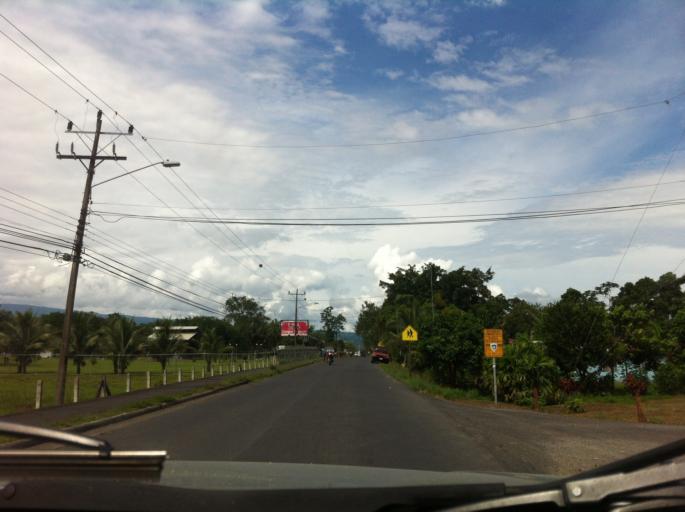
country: CR
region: Limon
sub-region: Canton de Pococi
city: Guapiles
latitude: 10.3203
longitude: -83.9213
